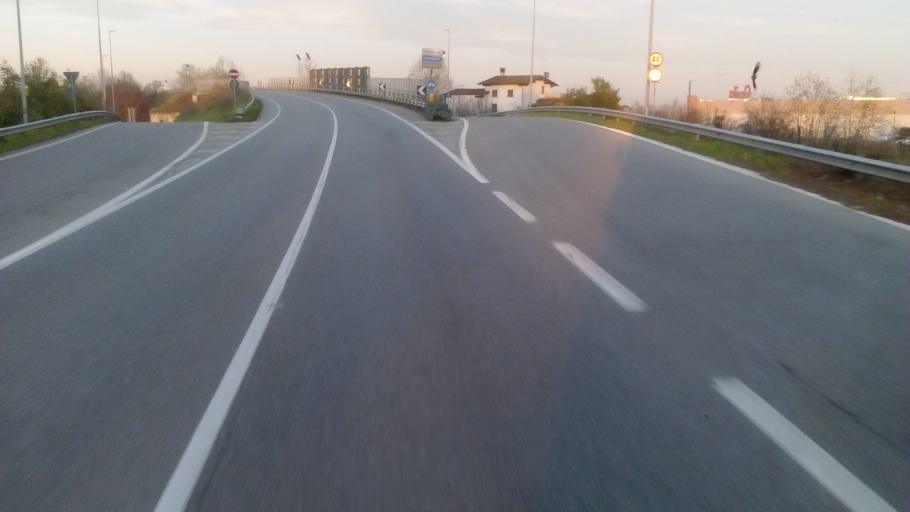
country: IT
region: Lombardy
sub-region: Provincia di Cremona
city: Soncino
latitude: 45.3900
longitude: 9.8548
